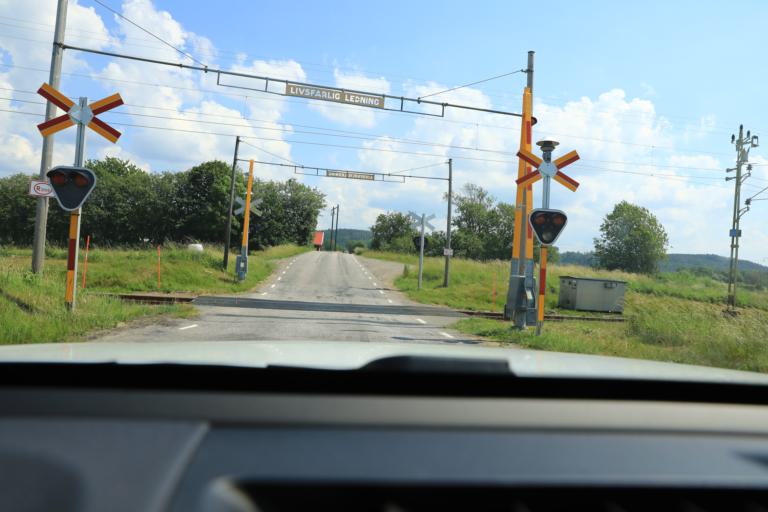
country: SE
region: Halland
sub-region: Varbergs Kommun
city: Veddige
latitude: 57.2077
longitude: 12.3116
